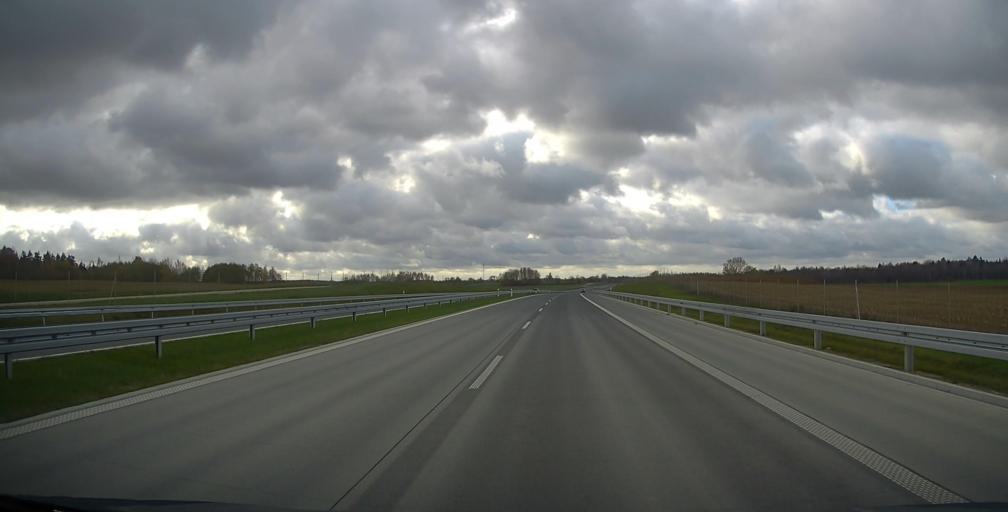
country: PL
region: Podlasie
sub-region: Powiat suwalski
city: Raczki
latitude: 53.9213
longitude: 22.7449
